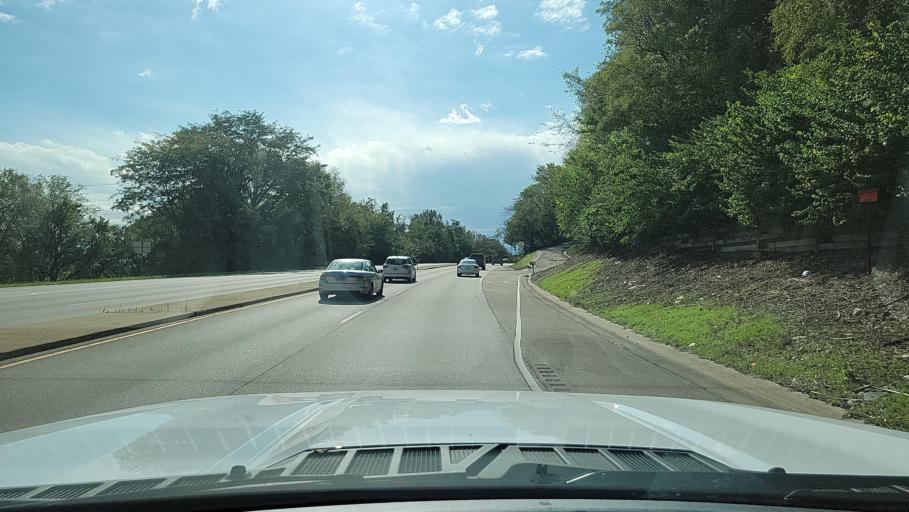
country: US
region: Illinois
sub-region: Tazewell County
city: Pekin
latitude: 40.5889
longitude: -89.6792
